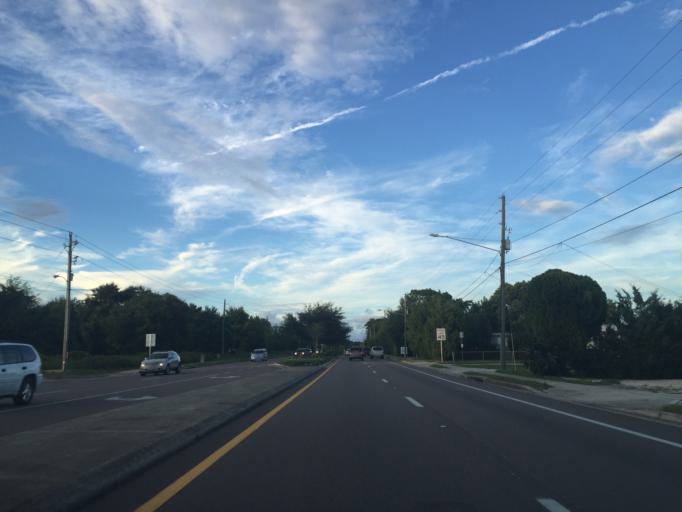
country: US
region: Florida
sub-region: Lake County
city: Tavares
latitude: 28.7920
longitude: -81.7450
